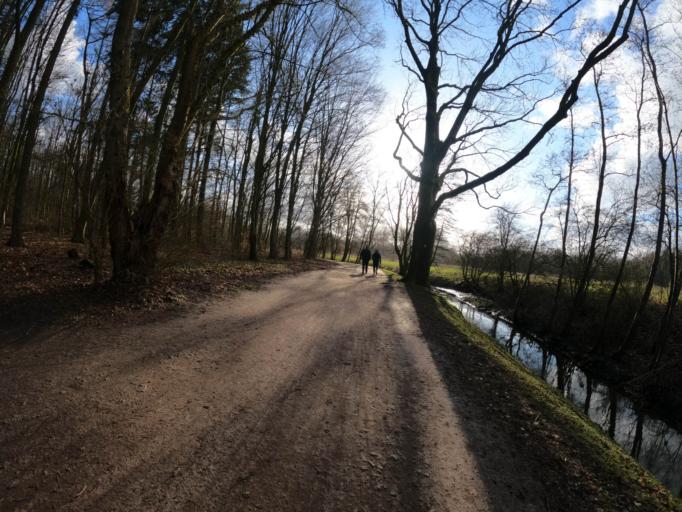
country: DE
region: Hamburg
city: Eidelstedt
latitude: 53.6219
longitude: 9.9298
